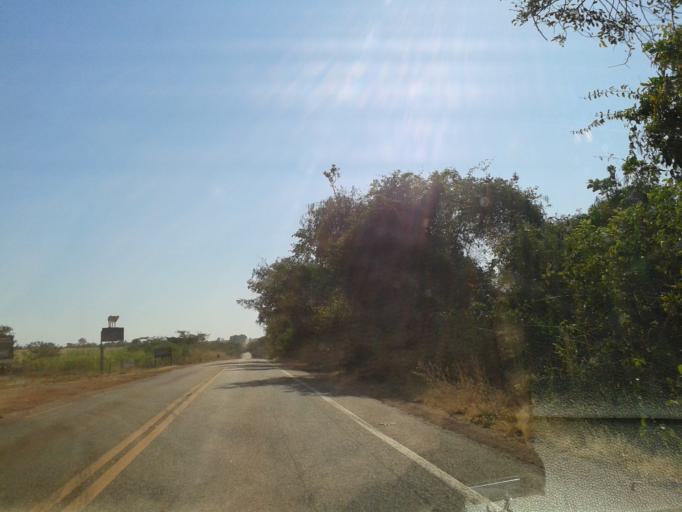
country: BR
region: Goias
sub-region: Mozarlandia
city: Mozarlandia
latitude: -14.4107
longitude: -50.4467
